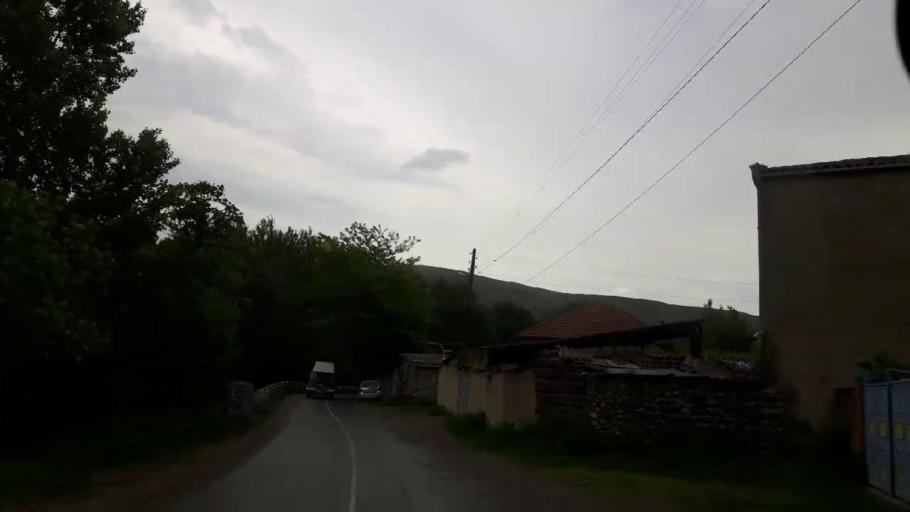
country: GE
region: Shida Kartli
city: Gori
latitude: 41.9655
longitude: 44.2190
